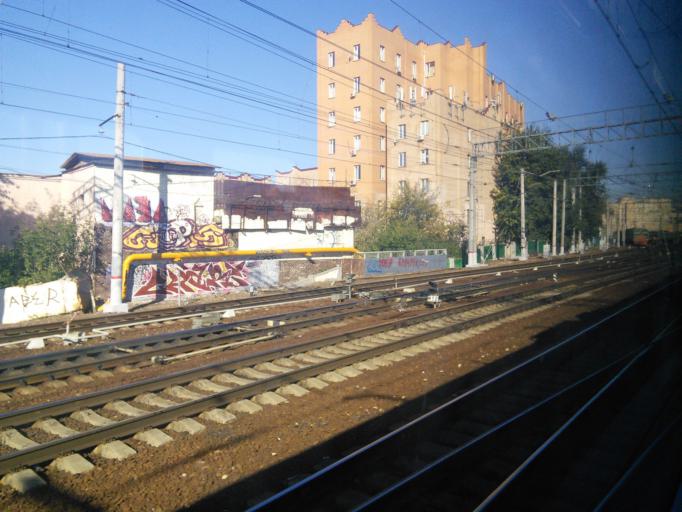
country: RU
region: Moscow
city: Taganskiy
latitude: 55.7529
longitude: 37.6665
